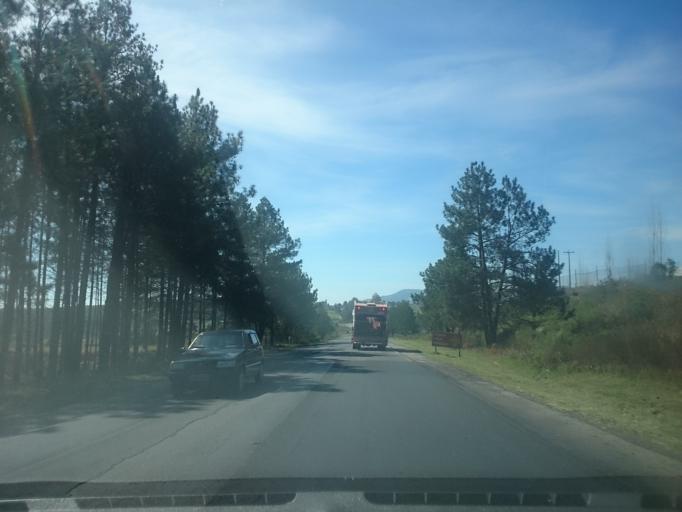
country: BR
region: Santa Catarina
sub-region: Lages
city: Lages
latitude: -27.7748
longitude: -50.2090
